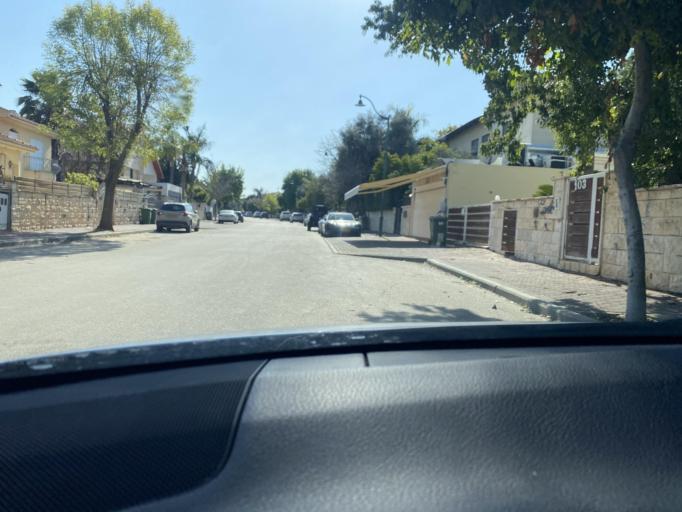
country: IL
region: Central District
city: Jaljulya
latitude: 32.1352
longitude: 34.9224
